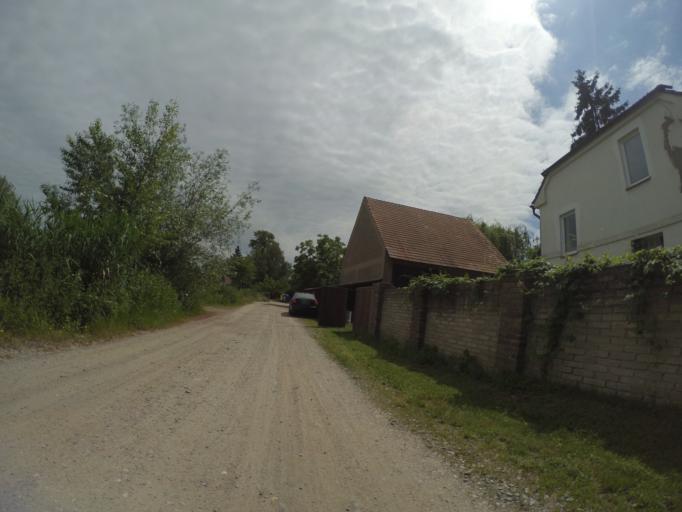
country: CZ
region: Central Bohemia
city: Lysa nad Labem
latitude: 50.1773
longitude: 14.8567
